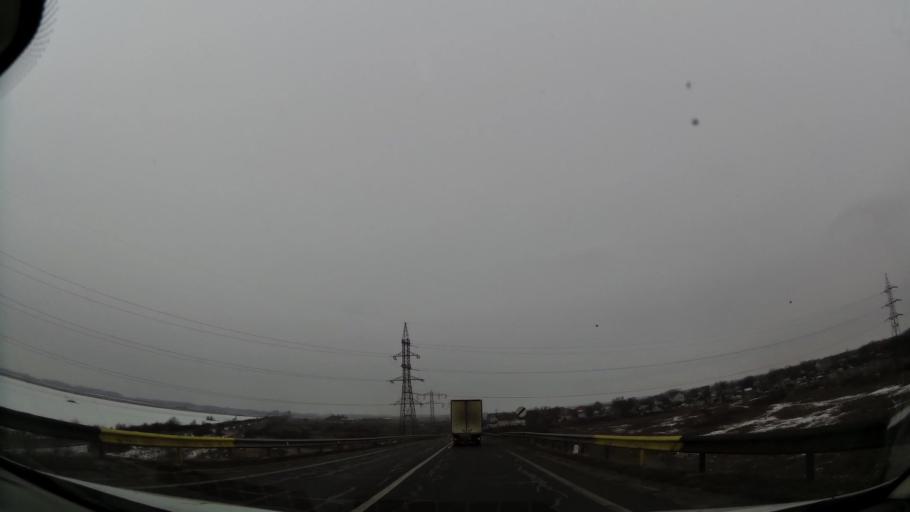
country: RO
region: Dambovita
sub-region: Comuna Contesti
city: Balteni
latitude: 44.6484
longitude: 25.6964
